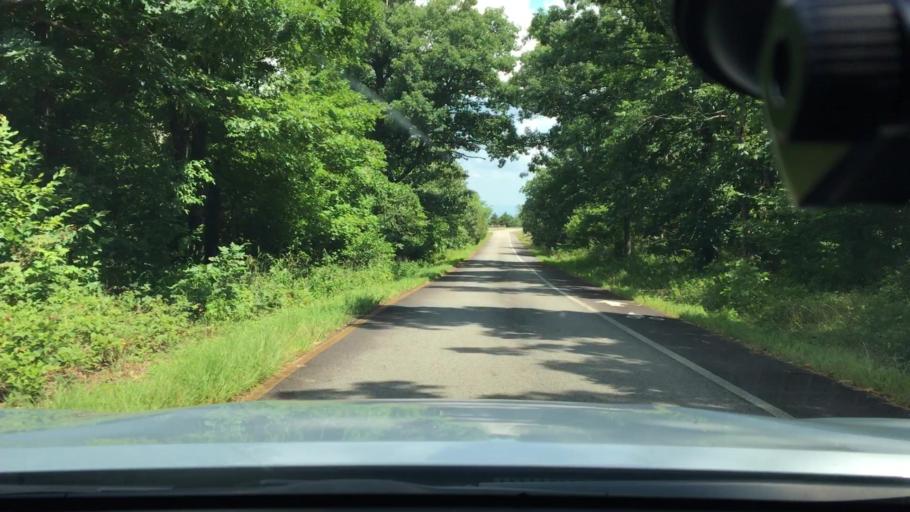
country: US
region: Arkansas
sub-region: Logan County
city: Paris
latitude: 35.1701
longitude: -93.6478
